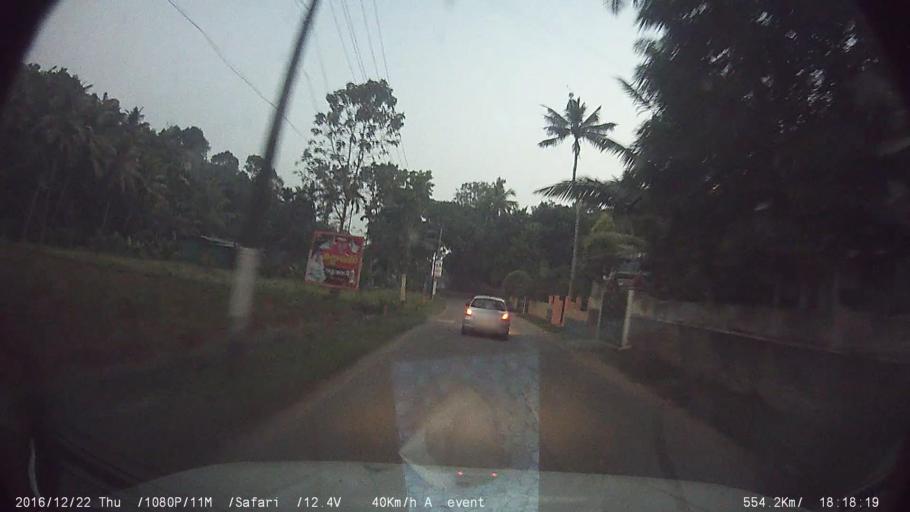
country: IN
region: Kerala
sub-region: Kottayam
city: Palackattumala
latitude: 9.7553
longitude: 76.6088
